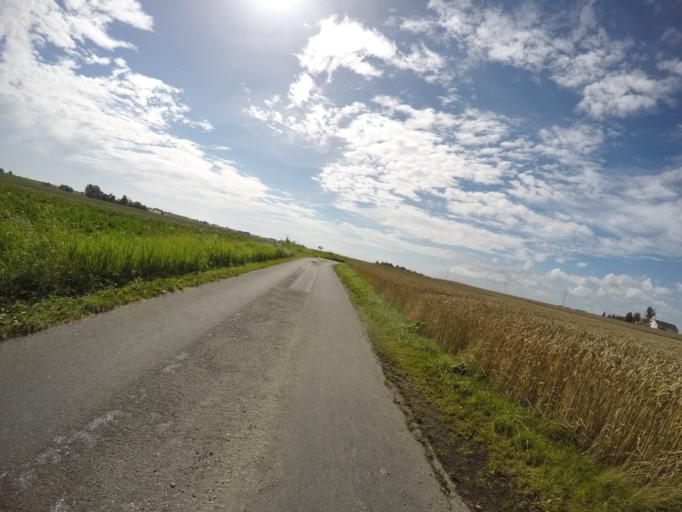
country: SE
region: Skane
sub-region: Tomelilla Kommun
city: Tomelilla
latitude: 55.4604
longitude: 14.1432
